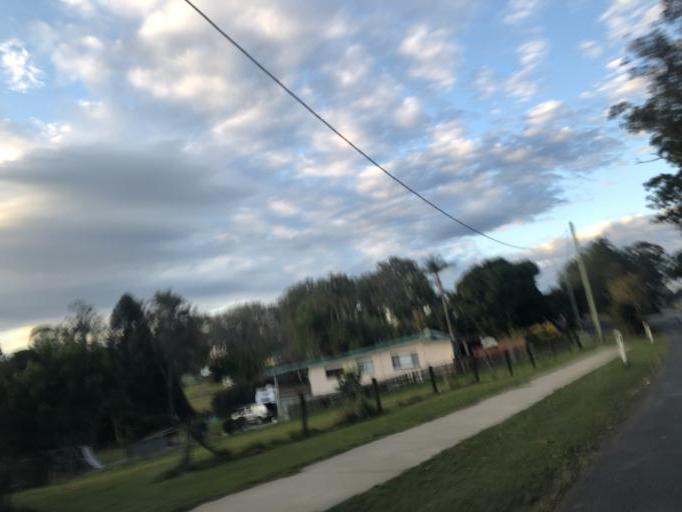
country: AU
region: New South Wales
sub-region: Nambucca Shire
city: Macksville
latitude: -30.7297
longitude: 152.9147
